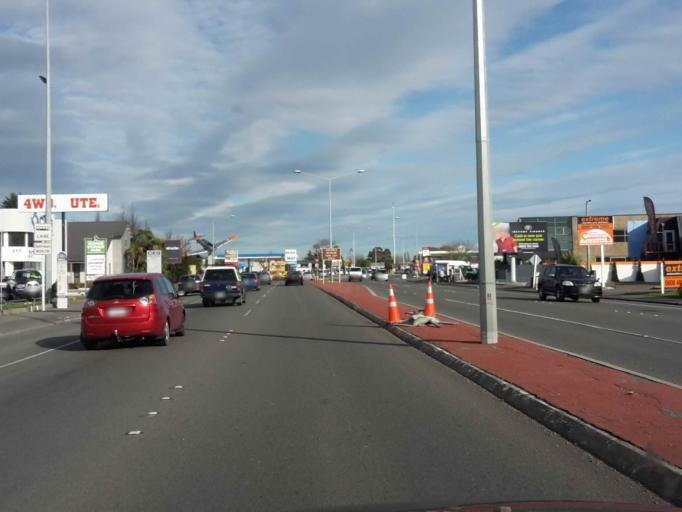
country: NZ
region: Canterbury
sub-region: Selwyn District
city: Prebbleton
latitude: -43.5421
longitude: 172.5483
